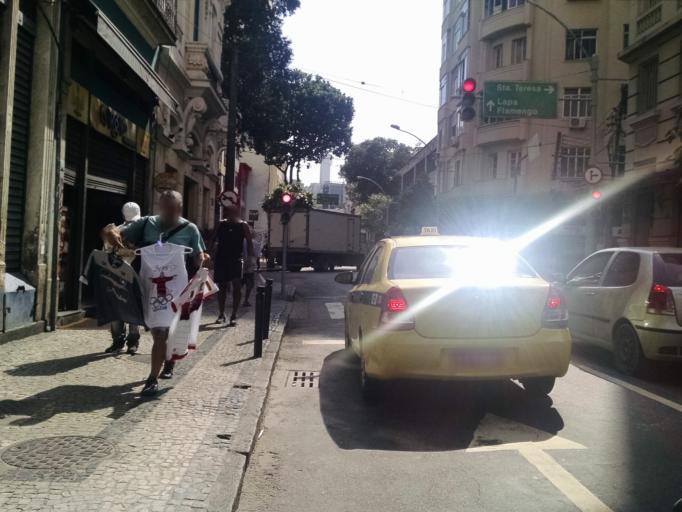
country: BR
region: Rio de Janeiro
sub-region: Rio De Janeiro
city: Rio de Janeiro
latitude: -22.9143
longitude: -43.1836
